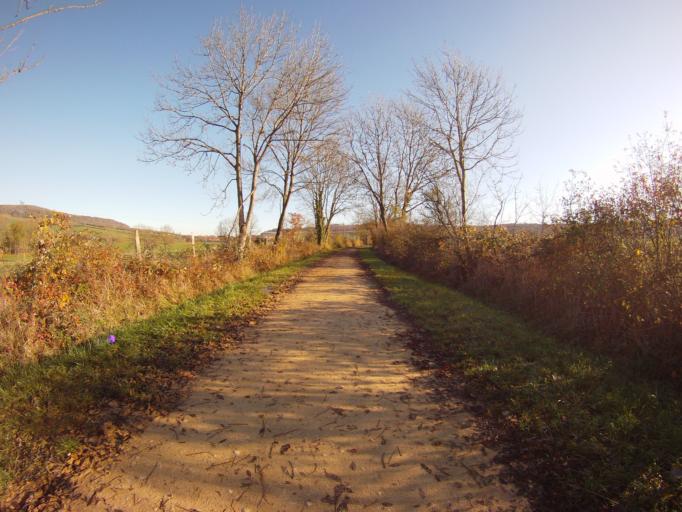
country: FR
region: Lorraine
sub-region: Departement de Meurthe-et-Moselle
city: Faulx
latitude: 48.7923
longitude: 6.2155
